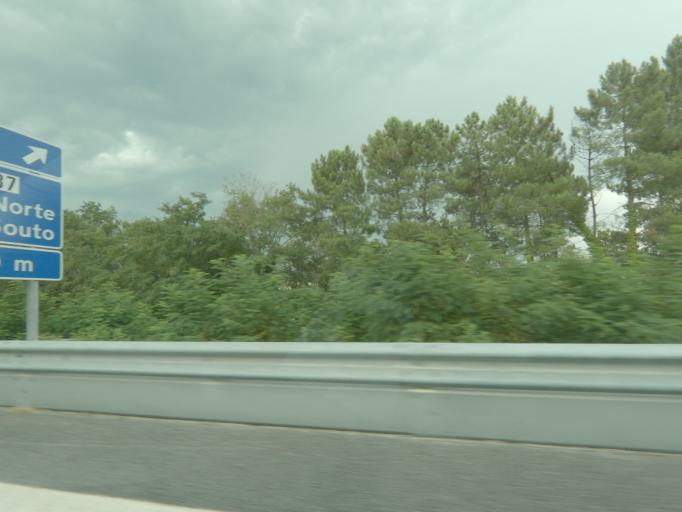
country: PT
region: Viseu
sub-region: Viseu
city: Abraveses
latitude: 40.6583
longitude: -7.9676
